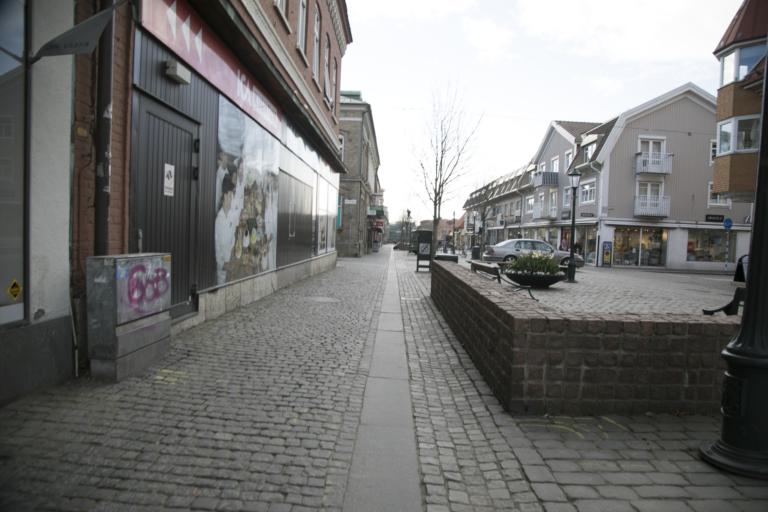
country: SE
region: Halland
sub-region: Varbergs Kommun
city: Varberg
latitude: 57.1054
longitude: 12.2534
